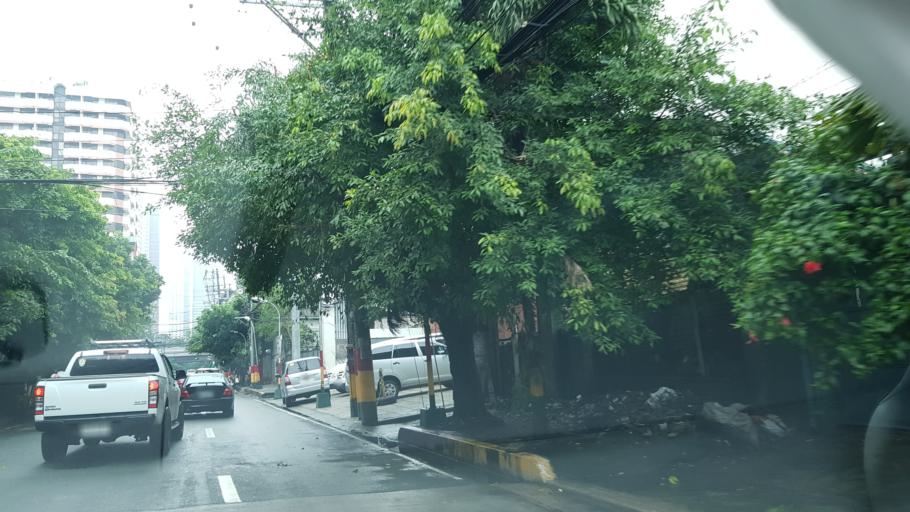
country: PH
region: Metro Manila
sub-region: City of Manila
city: Quiapo
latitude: 14.5807
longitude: 120.9878
